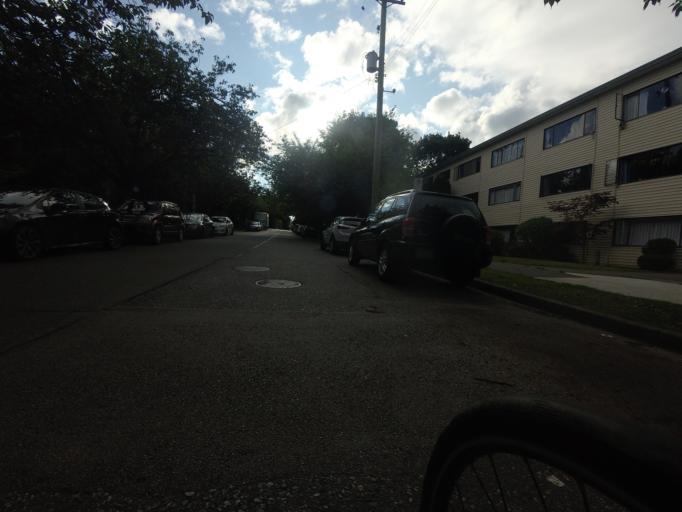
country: CA
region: British Columbia
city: West End
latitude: 49.2655
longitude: -123.1492
